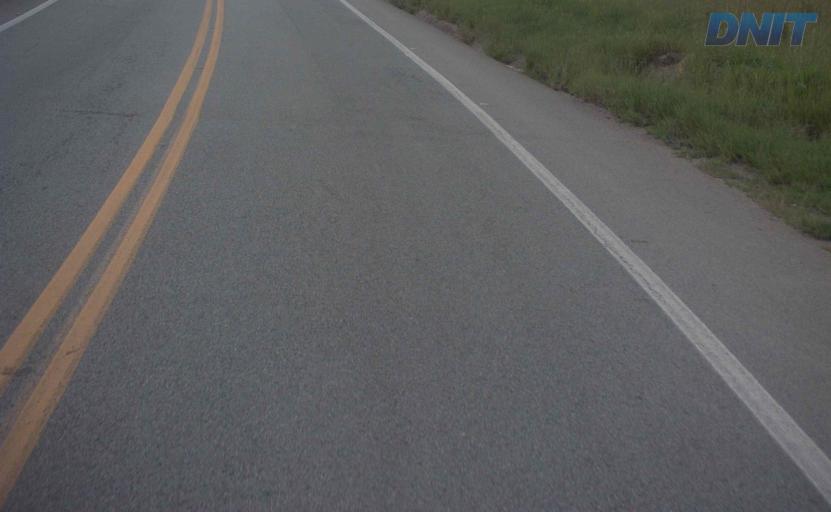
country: BR
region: Minas Gerais
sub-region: Nova Era
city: Nova Era
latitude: -19.6622
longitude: -42.9642
